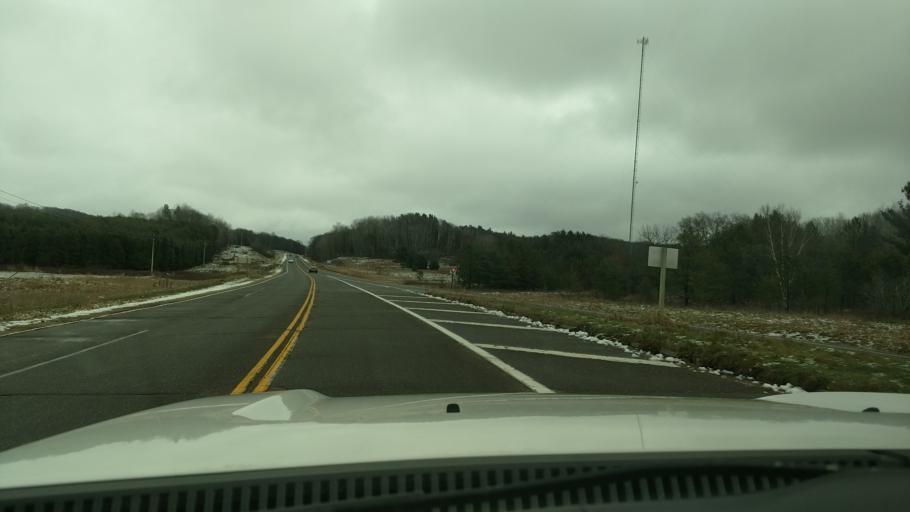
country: US
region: Wisconsin
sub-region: Dunn County
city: Tainter Lake
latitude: 45.1250
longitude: -91.9136
